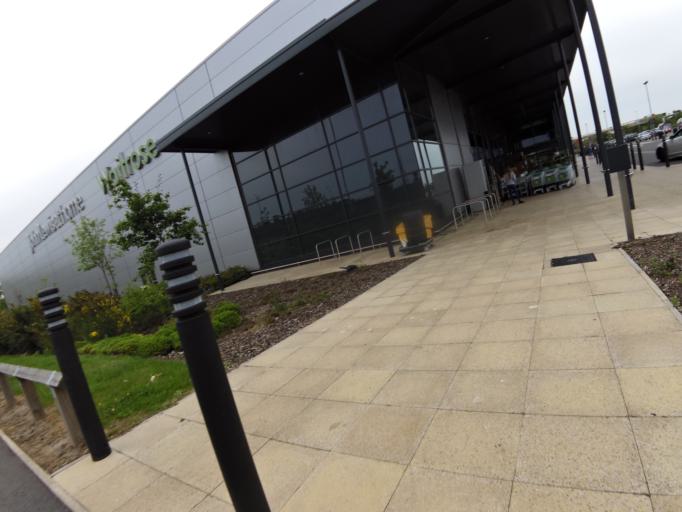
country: GB
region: England
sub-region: Suffolk
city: Kesgrave
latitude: 52.0346
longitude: 1.2035
